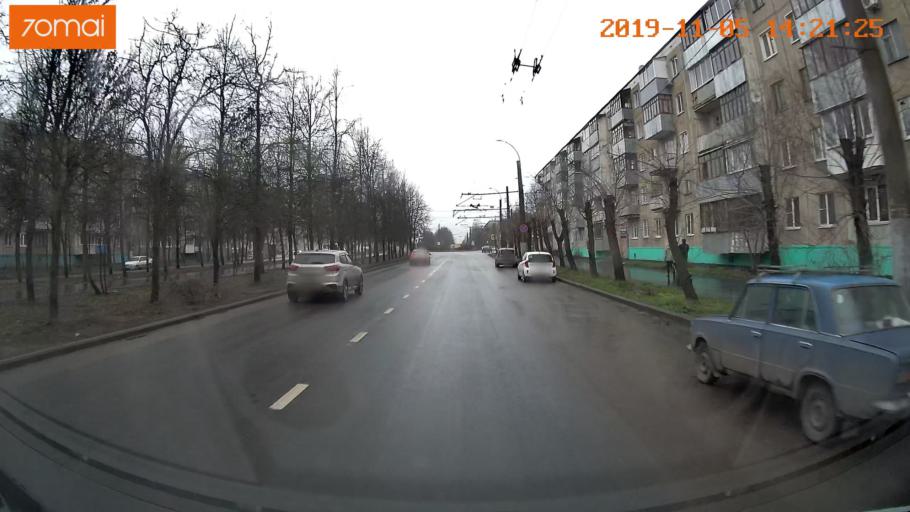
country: RU
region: Ivanovo
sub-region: Gorod Ivanovo
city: Ivanovo
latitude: 56.9593
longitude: 41.0109
